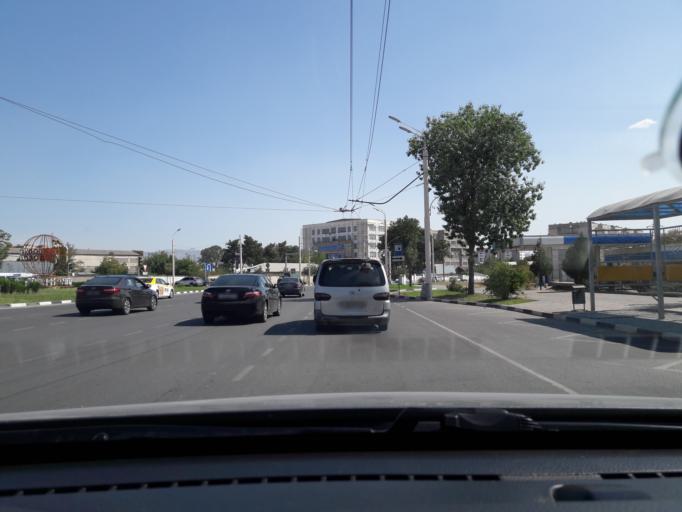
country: TJ
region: Dushanbe
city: Dushanbe
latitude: 38.5373
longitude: 68.7408
